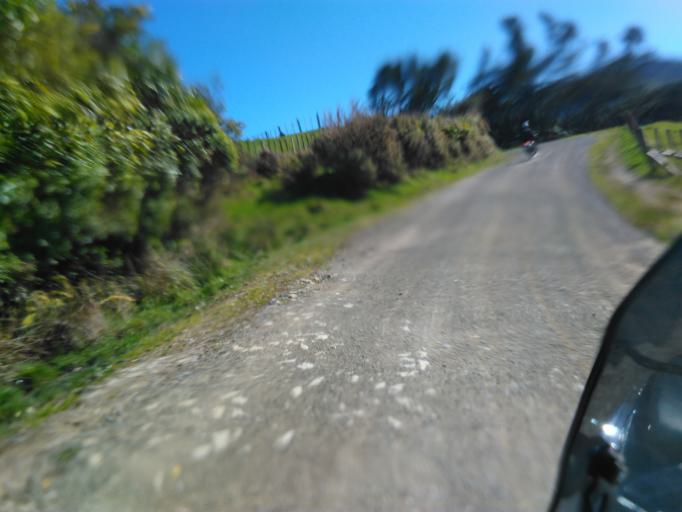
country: NZ
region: Bay of Plenty
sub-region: Opotiki District
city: Opotiki
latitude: -38.3556
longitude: 177.5897
